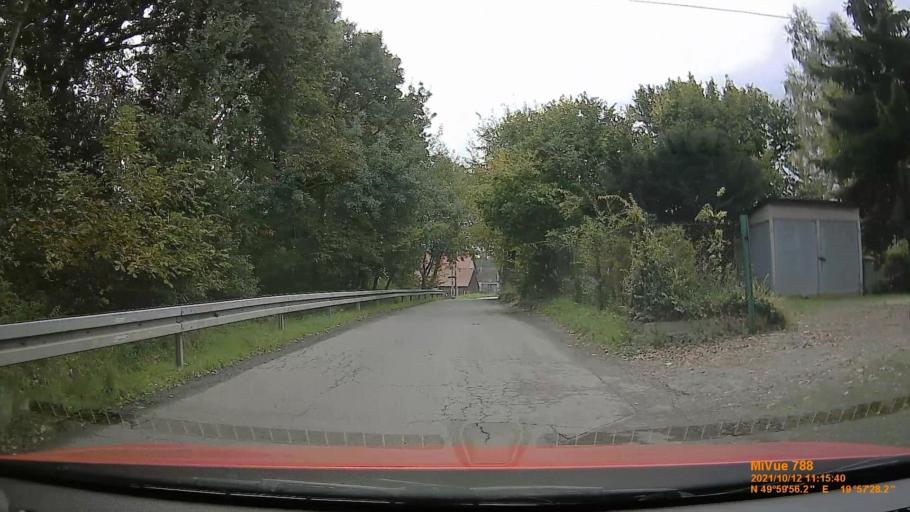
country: PL
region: Lesser Poland Voivodeship
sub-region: Powiat krakowski
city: Wrzasowice
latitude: 49.9989
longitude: 19.9579
